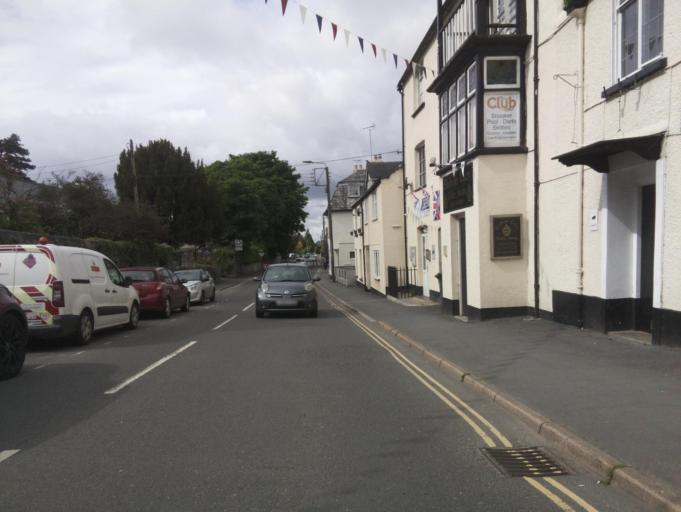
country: GB
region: England
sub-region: Devon
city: Chudleigh
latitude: 50.6036
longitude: -3.6028
